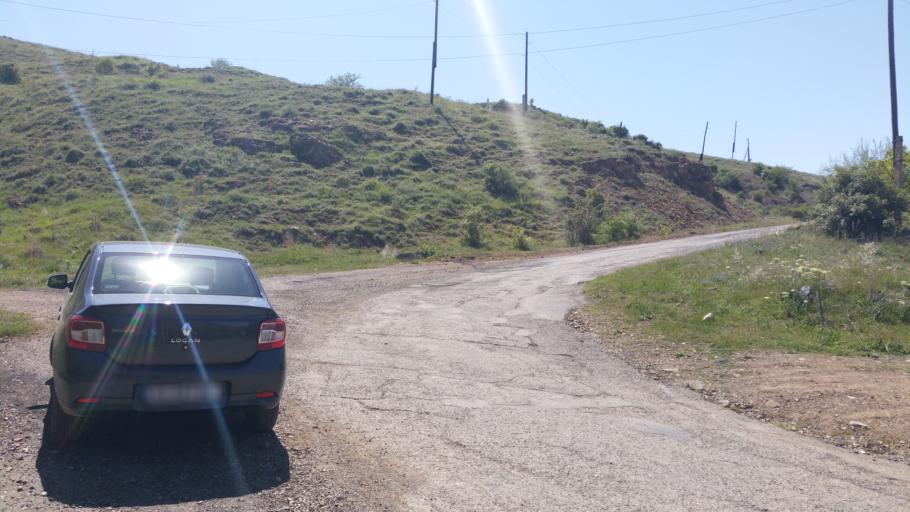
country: AM
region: Vayots' Dzori Marz
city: Vernashen
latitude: 39.7921
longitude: 45.3646
